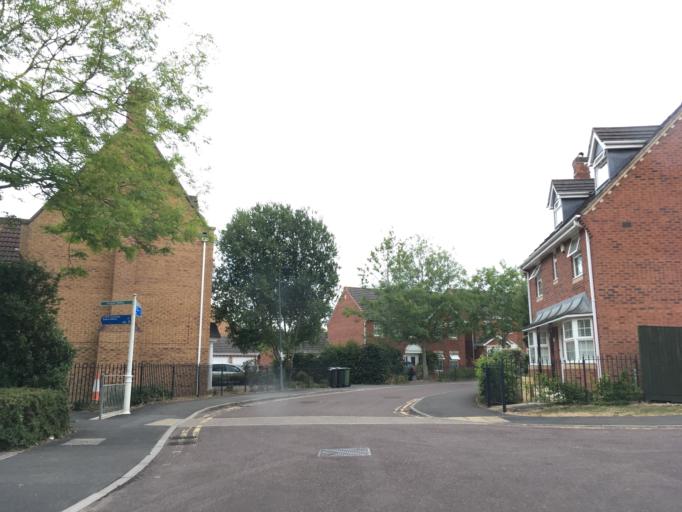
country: GB
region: England
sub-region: South Gloucestershire
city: Stoke Gifford
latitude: 51.4965
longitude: -2.5487
